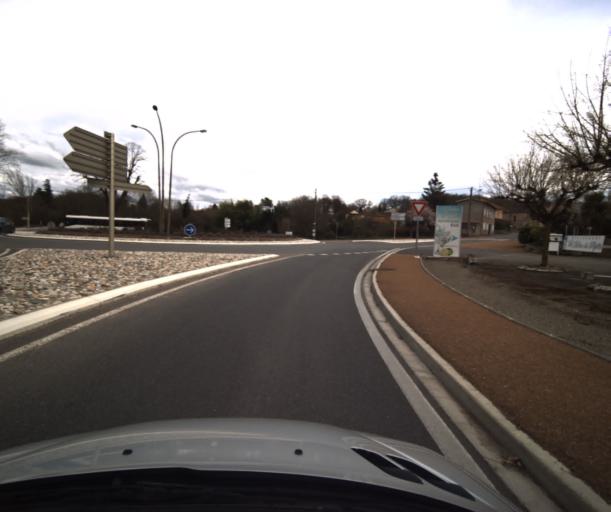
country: FR
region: Midi-Pyrenees
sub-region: Departement du Tarn-et-Garonne
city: Montricoux
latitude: 44.0730
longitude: 1.6145
